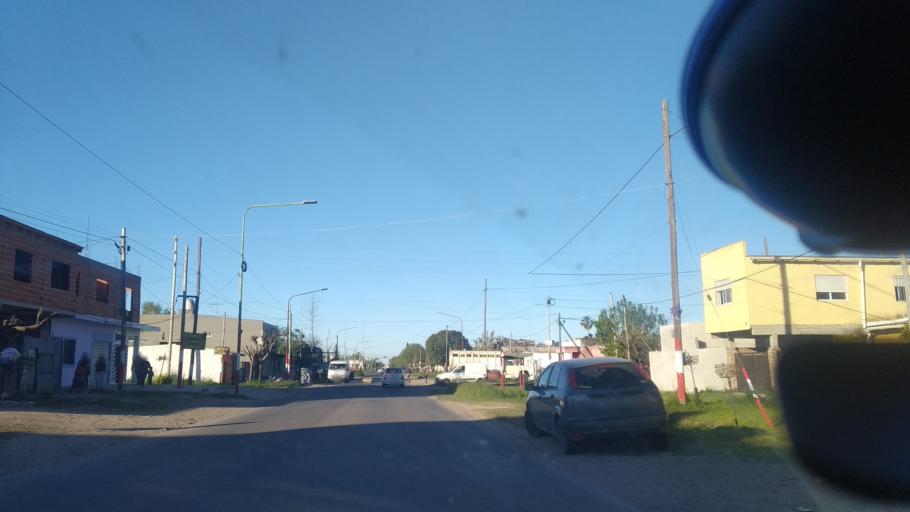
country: AR
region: Buenos Aires
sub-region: Partido de La Plata
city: La Plata
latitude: -34.9618
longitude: -57.9617
